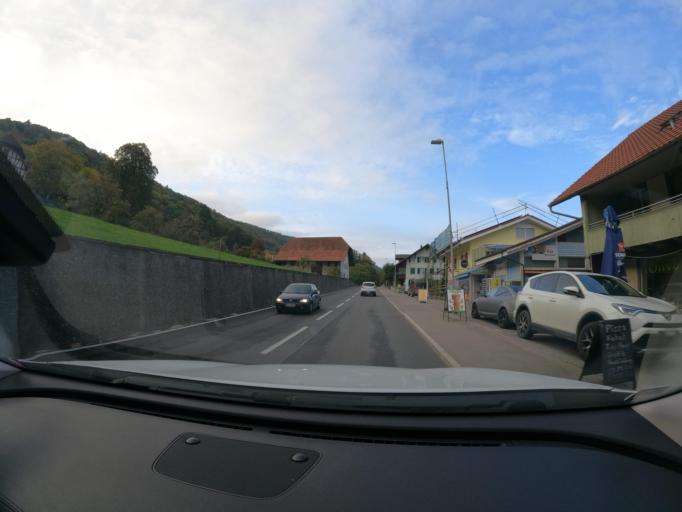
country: CH
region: Bern
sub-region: Bern-Mittelland District
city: Toffen
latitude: 46.8618
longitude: 7.4903
